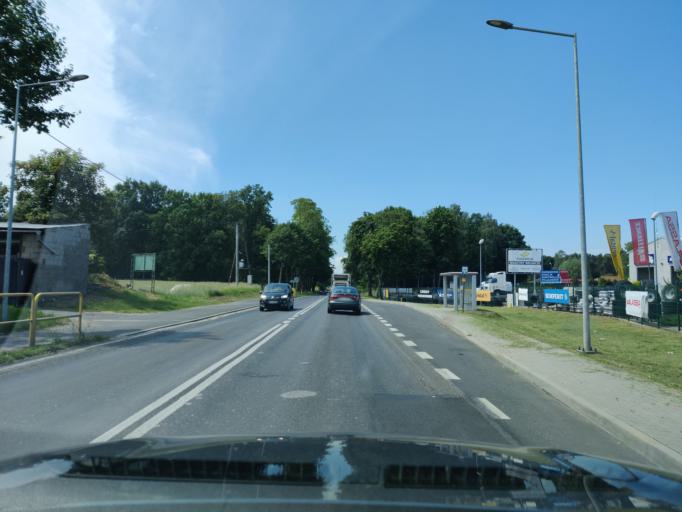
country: PL
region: Greater Poland Voivodeship
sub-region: Powiat grodziski
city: Rakoniewice
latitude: 52.1586
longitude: 16.3035
